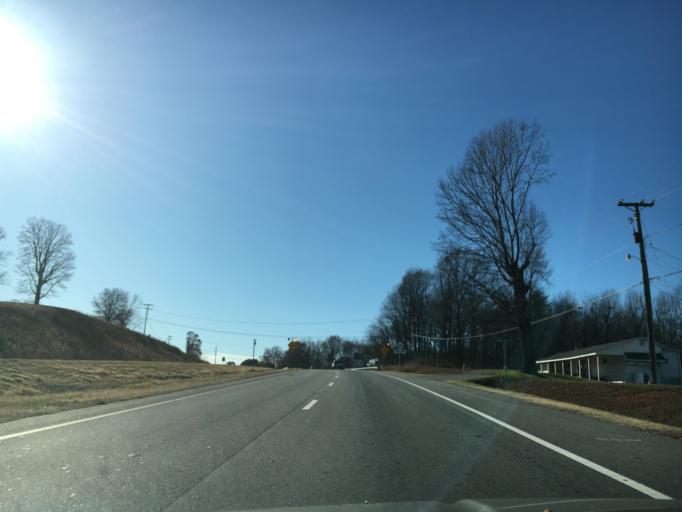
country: US
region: Virginia
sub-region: Henry County
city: Horse Pasture
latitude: 36.6408
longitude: -79.9298
